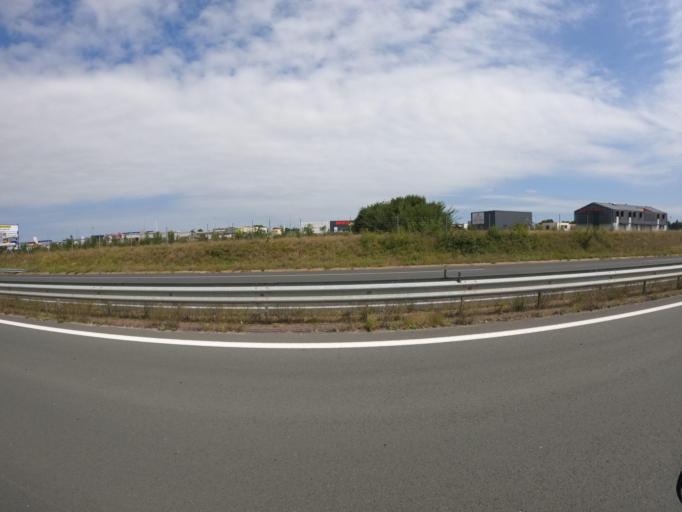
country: FR
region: Poitou-Charentes
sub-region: Departement de la Charente-Maritime
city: Saint-Jean-de-Liversay
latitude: 46.2260
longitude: -0.8715
